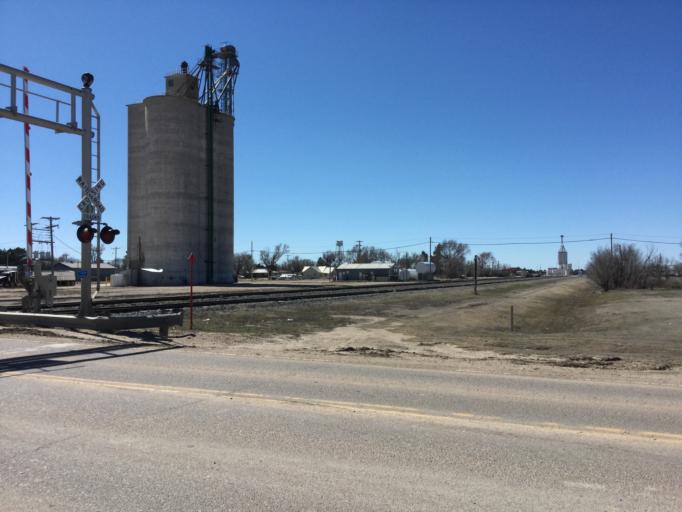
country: US
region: Kansas
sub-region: Wichita County
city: Leoti
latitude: 38.4858
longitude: -101.3584
